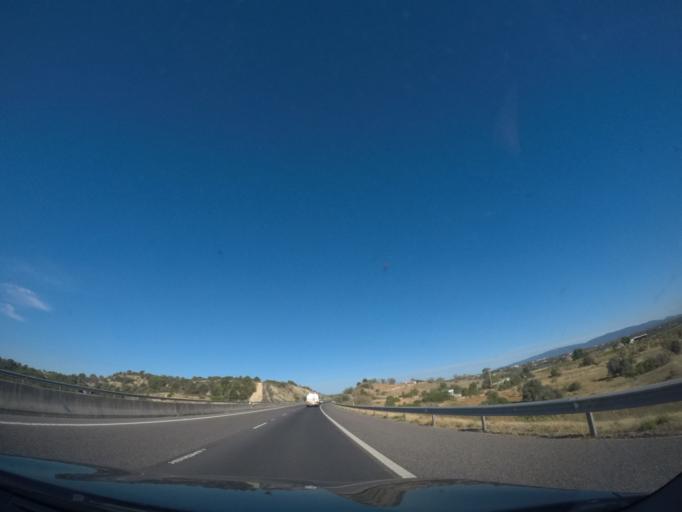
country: PT
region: Faro
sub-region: Lagoa
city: Lagoa
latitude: 37.1380
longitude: -8.4040
